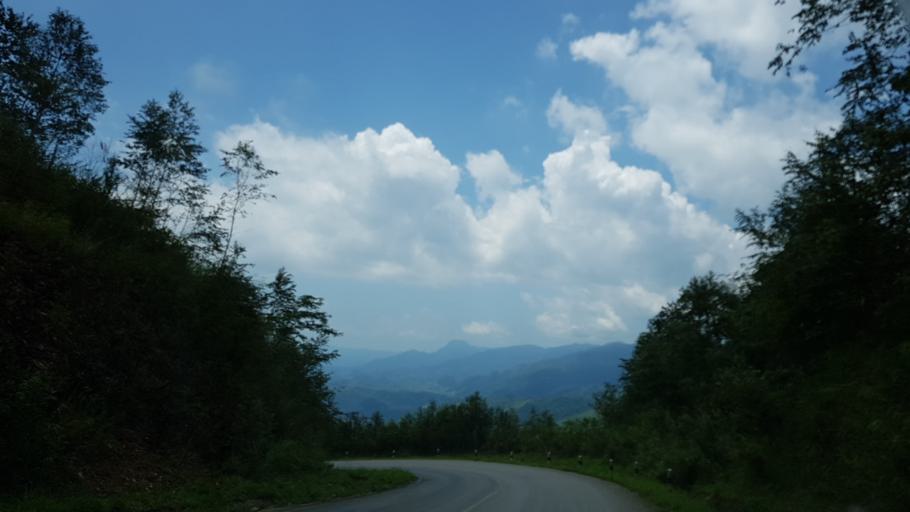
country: LA
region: Vientiane
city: Muang Kasi
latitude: 19.3789
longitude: 102.1570
